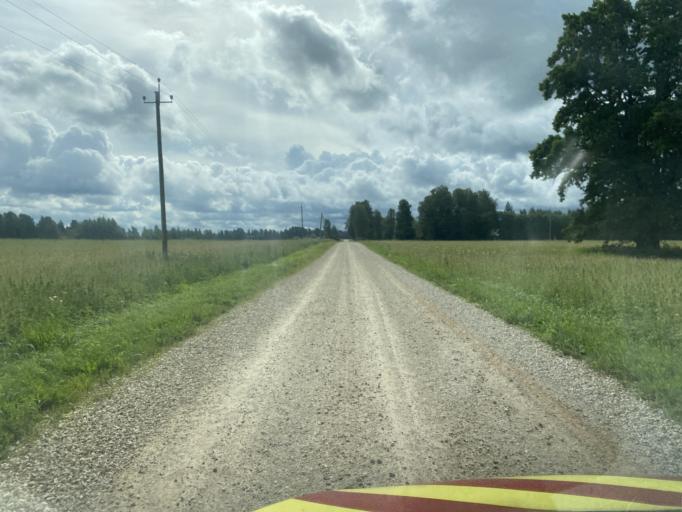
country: EE
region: Viljandimaa
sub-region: Karksi vald
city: Karksi-Nuia
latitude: 58.0672
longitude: 25.5248
